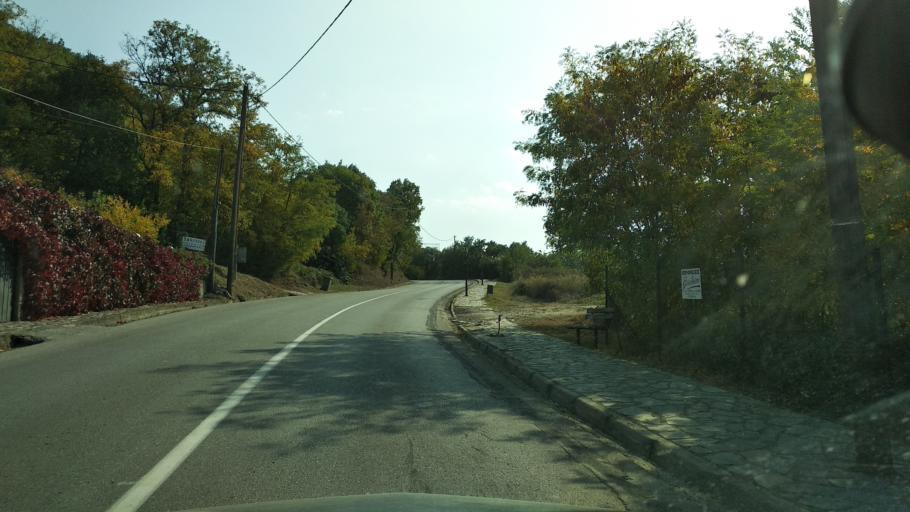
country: GR
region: Thessaly
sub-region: Trikala
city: Kastraki
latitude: 39.7121
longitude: 21.6159
